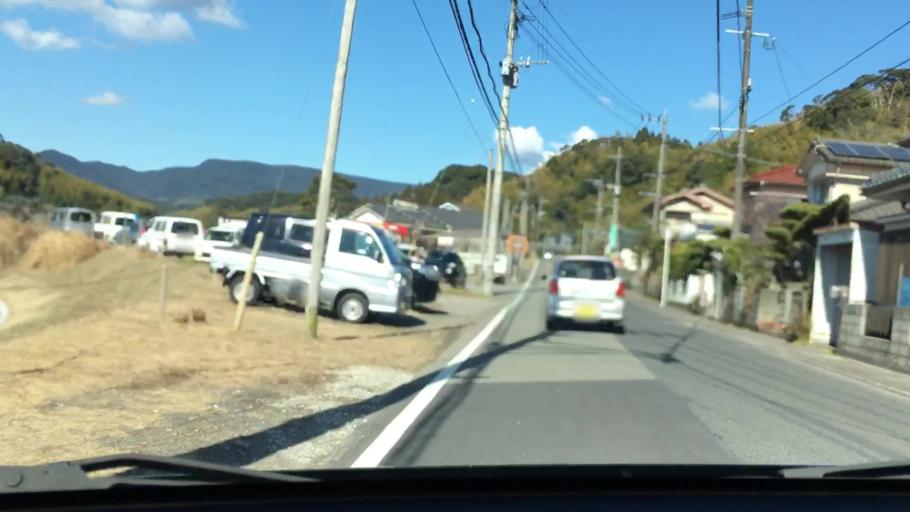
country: JP
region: Kagoshima
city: Ijuin
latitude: 31.6818
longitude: 130.4698
